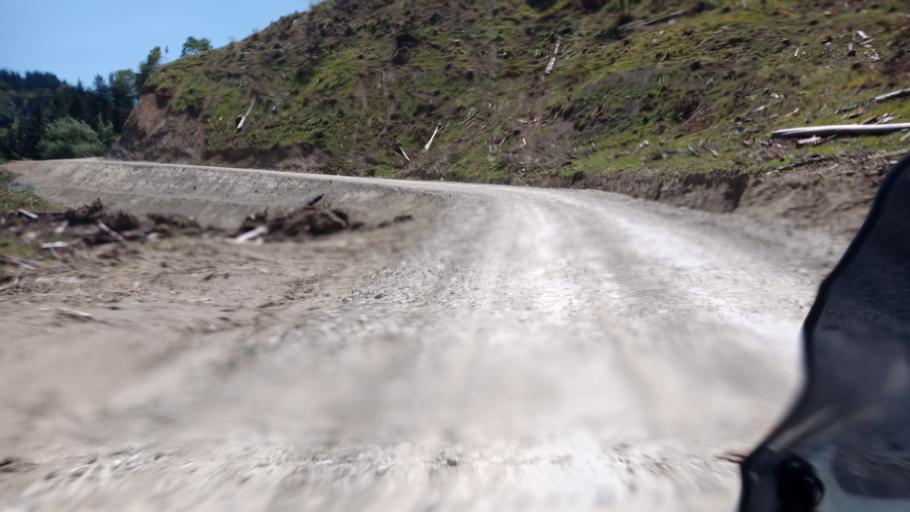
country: NZ
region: Gisborne
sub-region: Gisborne District
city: Gisborne
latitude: -38.2802
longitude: 177.9990
